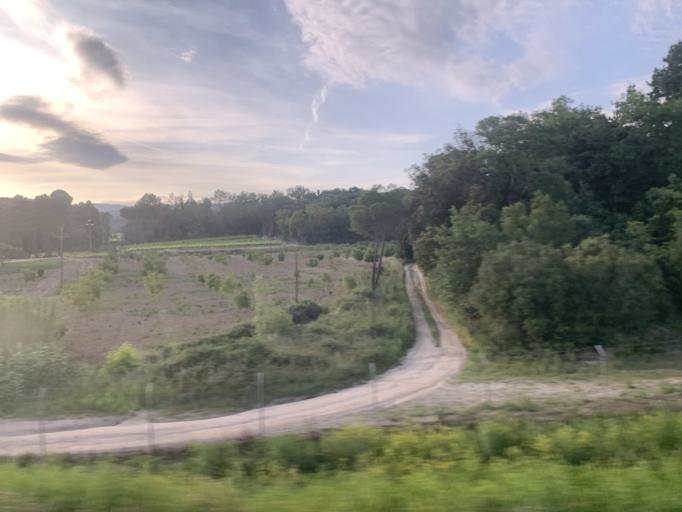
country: ES
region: Catalonia
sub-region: Provincia de Girona
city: Hostalric
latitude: 41.7504
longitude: 2.6426
